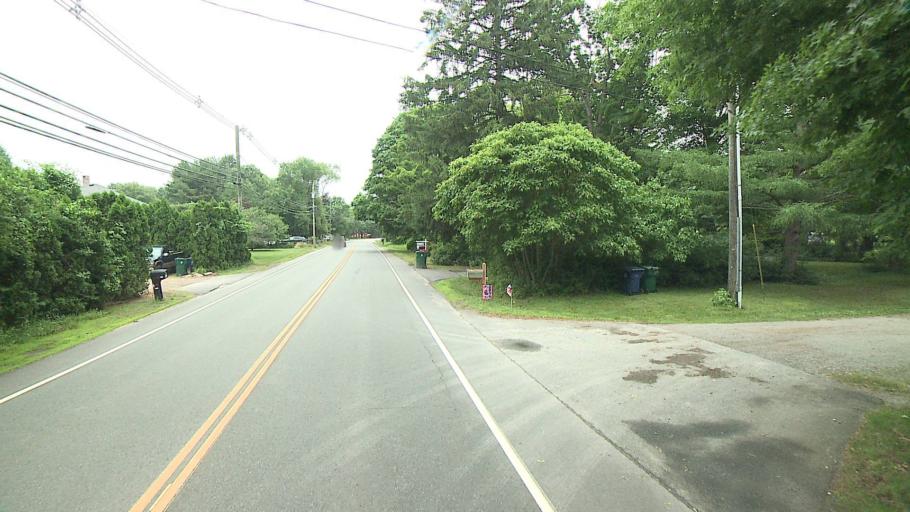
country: US
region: Connecticut
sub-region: Middlesex County
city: Old Saybrook Center
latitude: 41.3423
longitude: -72.3071
